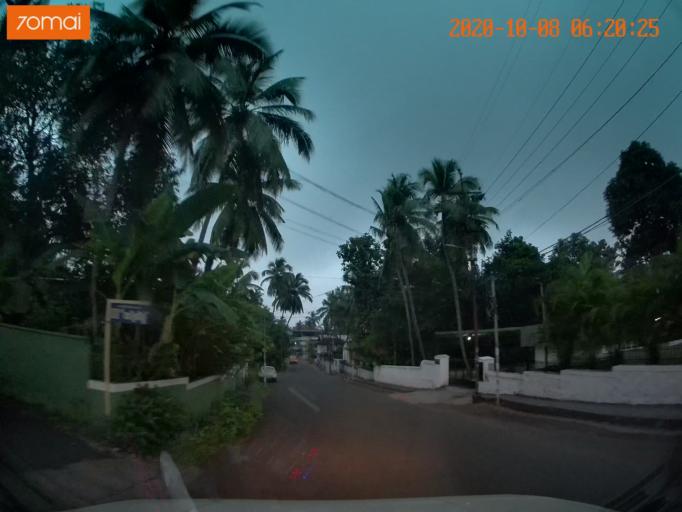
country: IN
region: Kerala
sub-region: Thrissur District
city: Trichur
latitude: 10.5181
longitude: 76.2362
